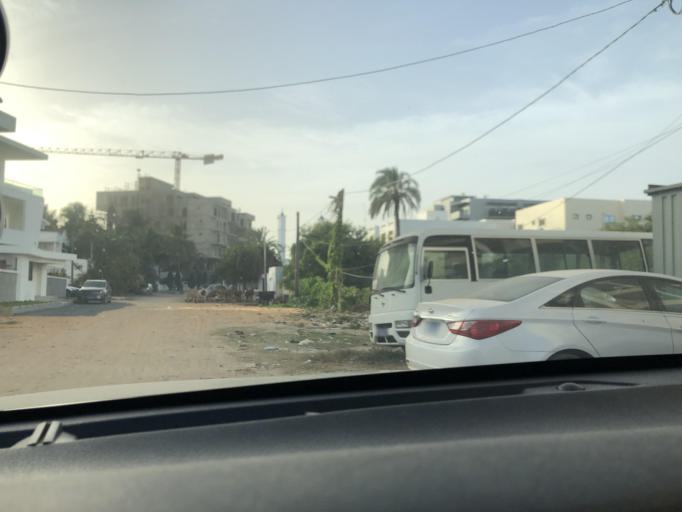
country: SN
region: Dakar
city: Mermoz Boabab
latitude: 14.7423
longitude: -17.5154
